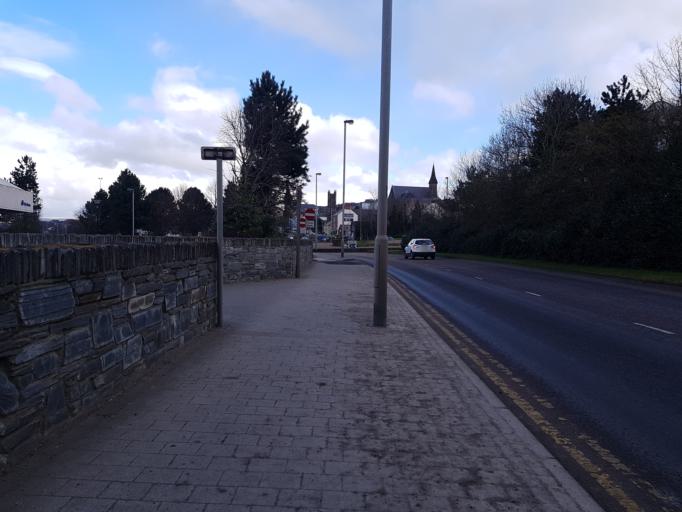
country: GB
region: Northern Ireland
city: Londonderry County Borough
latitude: 54.9916
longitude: -7.3134
